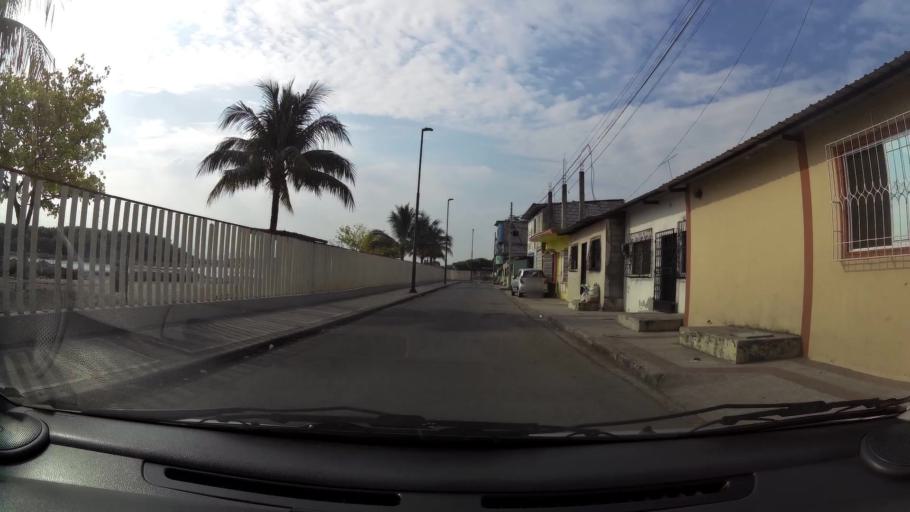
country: EC
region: Guayas
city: Guayaquil
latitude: -2.2468
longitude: -79.9086
